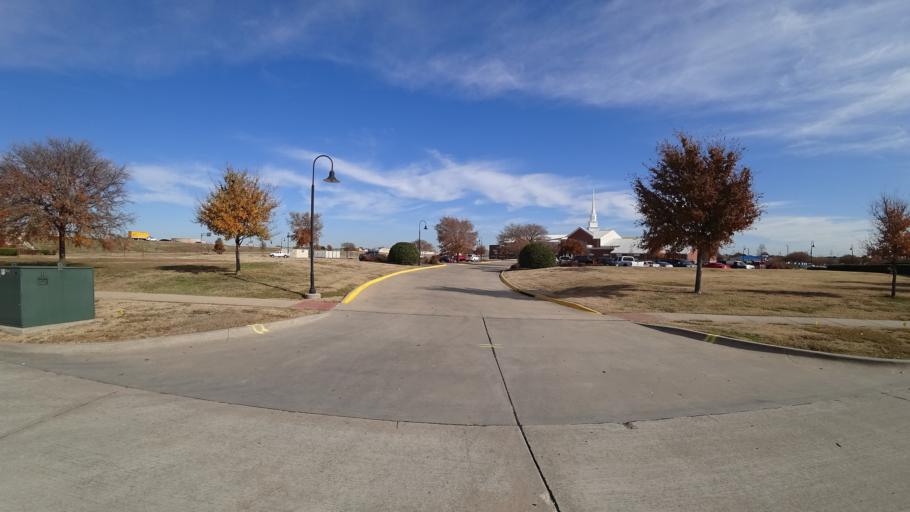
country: US
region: Texas
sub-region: Denton County
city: Lewisville
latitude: 33.0110
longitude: -96.9418
